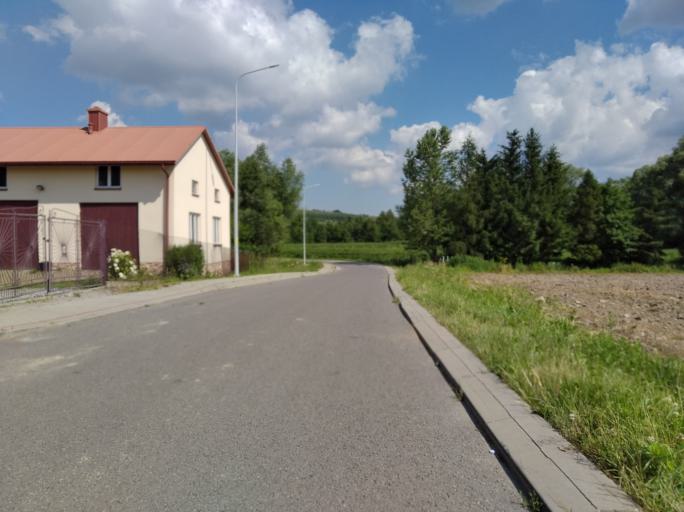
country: PL
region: Subcarpathian Voivodeship
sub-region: Powiat rzeszowski
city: Dynow
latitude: 49.8313
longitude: 22.2255
